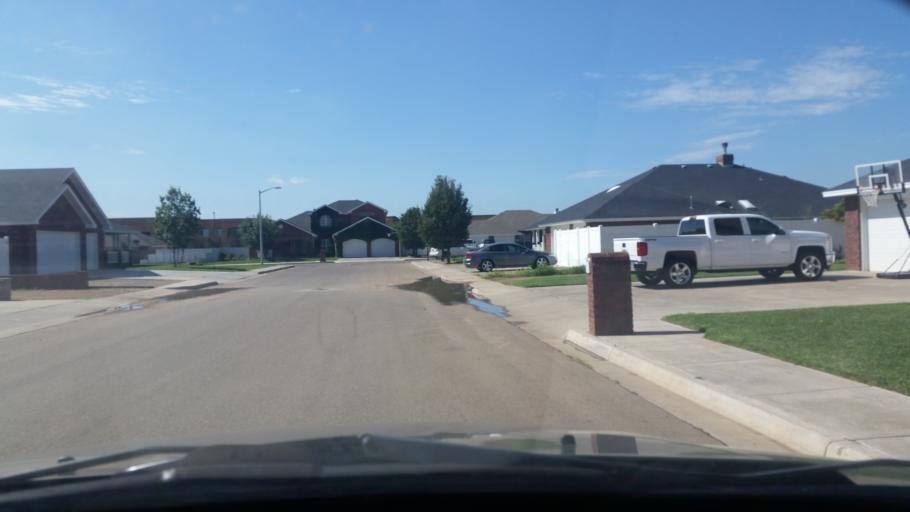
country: US
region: New Mexico
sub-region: Curry County
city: Clovis
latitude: 34.4370
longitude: -103.1756
